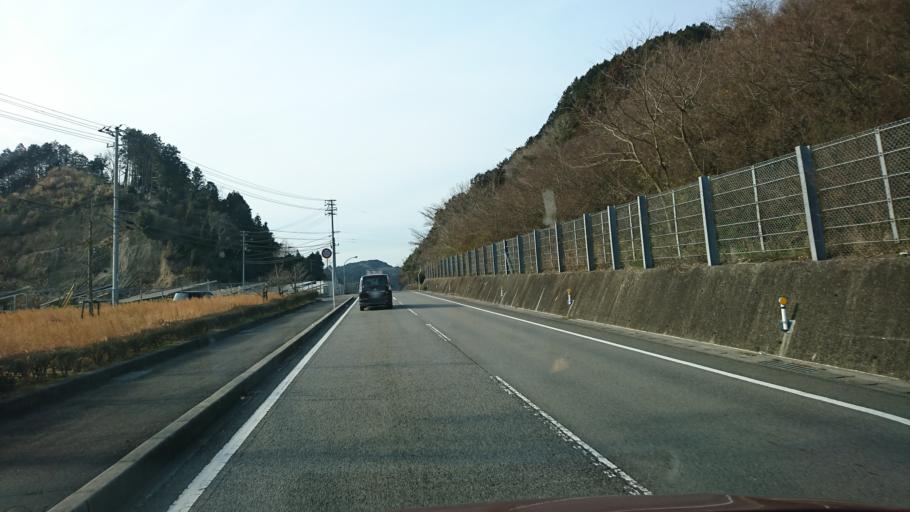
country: JP
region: Ehime
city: Hojo
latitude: 33.9943
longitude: 132.9281
